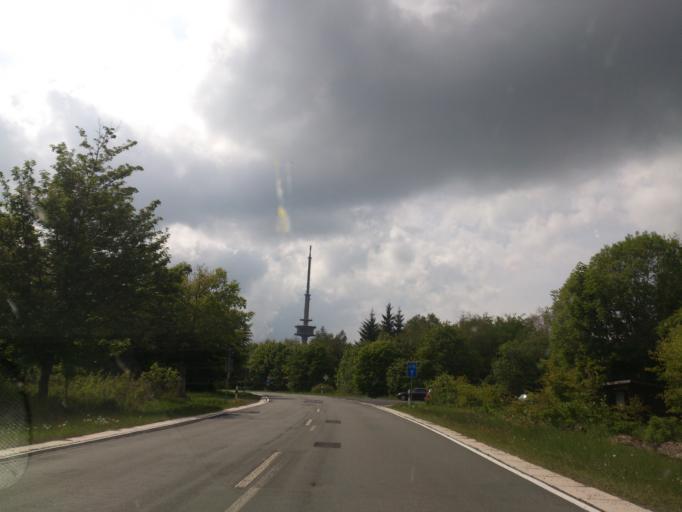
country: DE
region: Hesse
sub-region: Regierungsbezirk Kassel
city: Martinhagen
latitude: 51.3127
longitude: 9.3566
